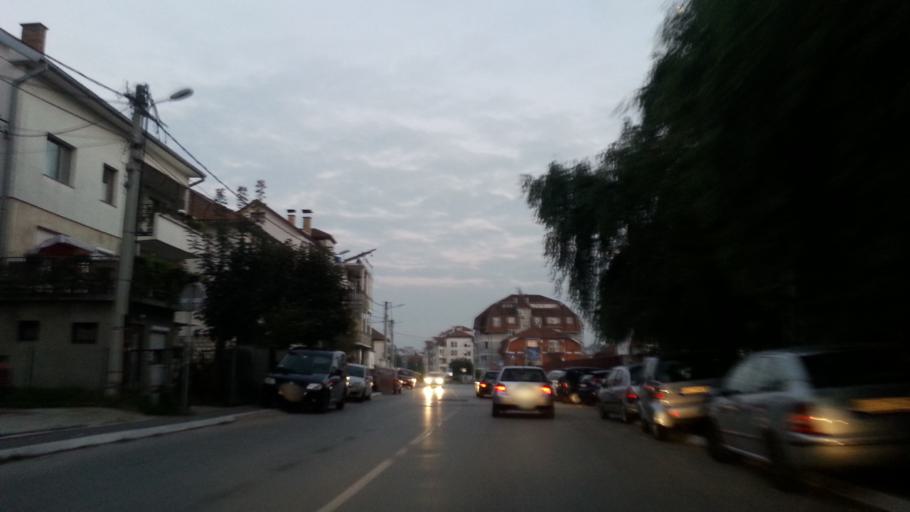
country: RS
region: Central Serbia
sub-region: Belgrade
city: Cukarica
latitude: 44.7594
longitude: 20.4198
